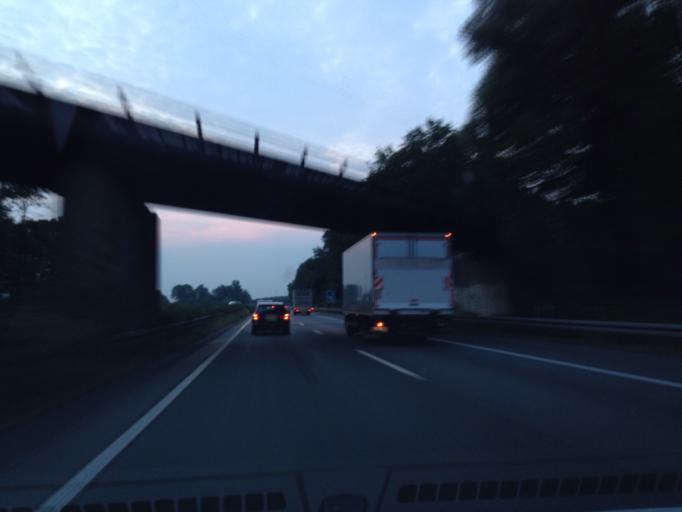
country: DE
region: North Rhine-Westphalia
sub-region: Regierungsbezirk Munster
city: Ascheberg
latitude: 51.8304
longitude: 7.5990
